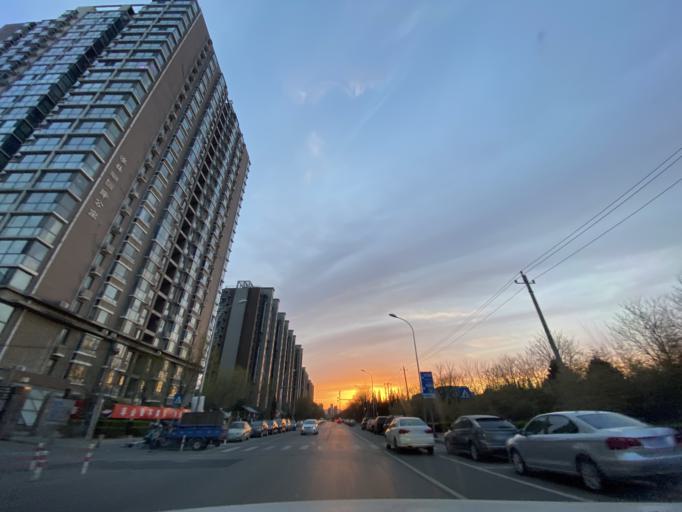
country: CN
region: Beijing
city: Qinghe
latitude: 40.0163
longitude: 116.3637
